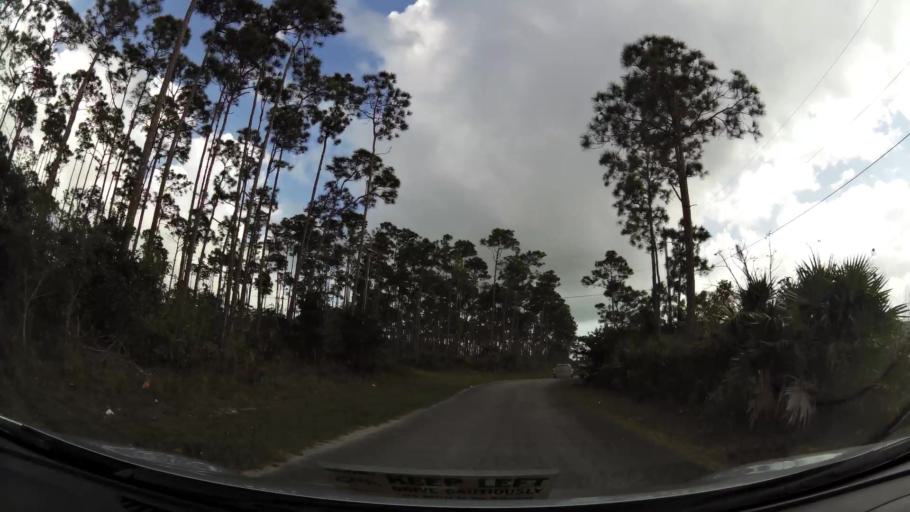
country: BS
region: Freeport
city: Freeport
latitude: 26.5226
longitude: -78.7238
